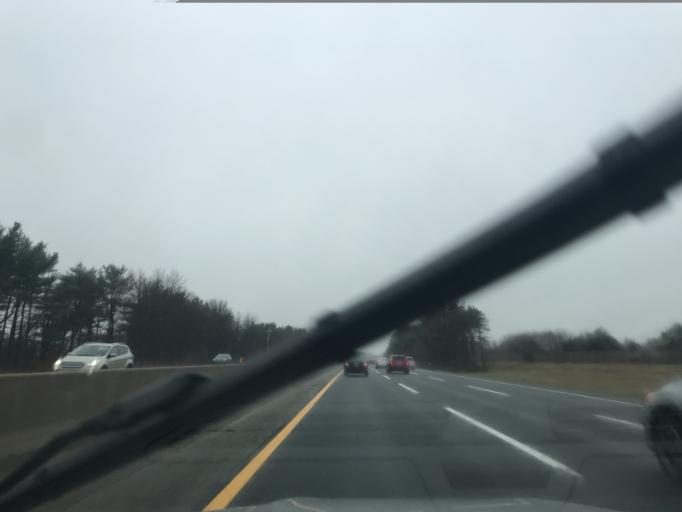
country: US
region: New Jersey
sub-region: Burlington County
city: Mount Laurel
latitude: 39.9652
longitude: -74.9101
